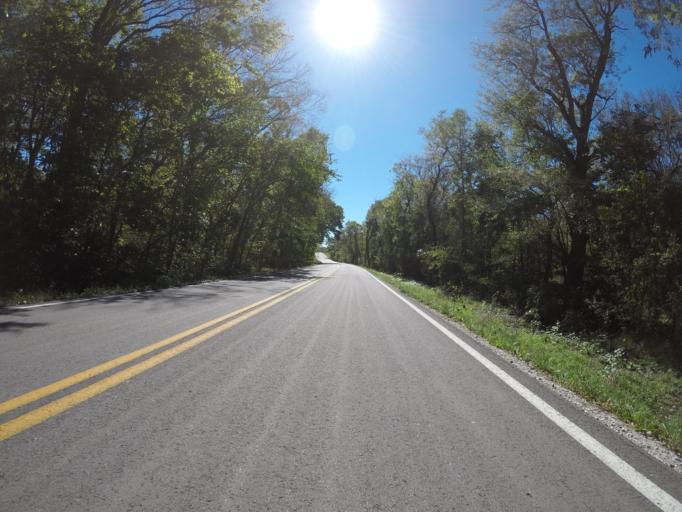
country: US
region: Kansas
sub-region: Johnson County
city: De Soto
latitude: 38.9650
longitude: -95.0194
